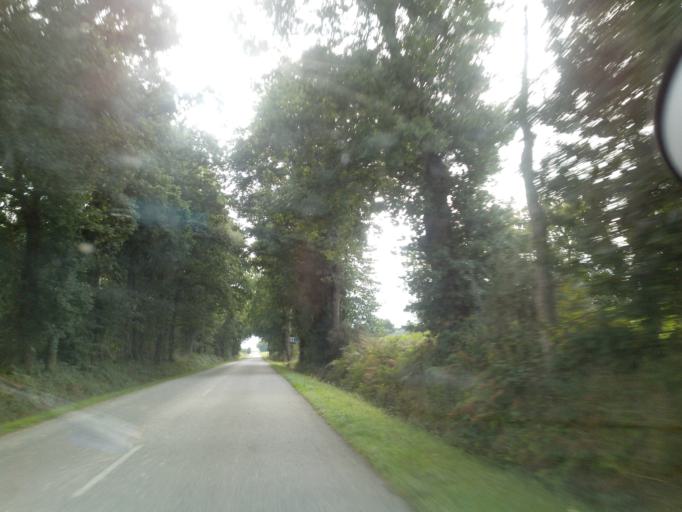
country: FR
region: Brittany
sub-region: Departement du Morbihan
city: Mauron
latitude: 48.1244
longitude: -2.2742
